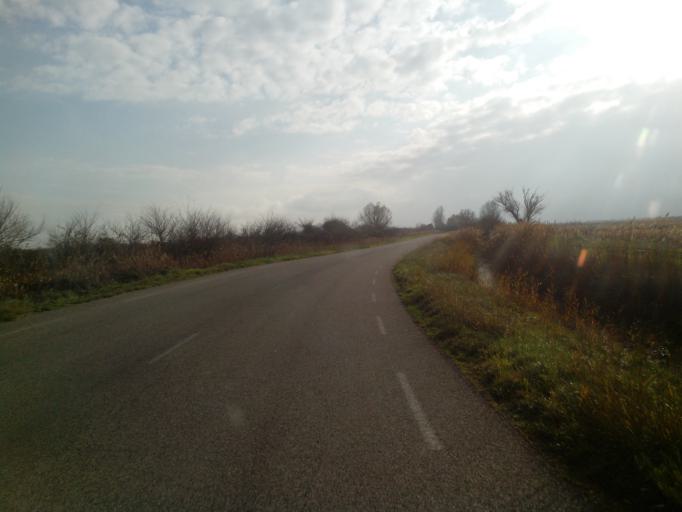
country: FR
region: Languedoc-Roussillon
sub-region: Departement du Gard
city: Saint-Gilles
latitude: 43.6036
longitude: 4.4891
